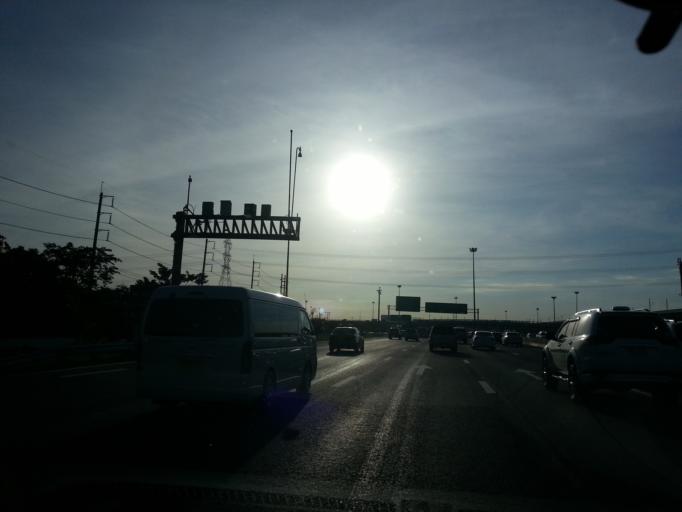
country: TH
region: Bangkok
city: Saphan Sung
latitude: 13.7333
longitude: 100.6975
